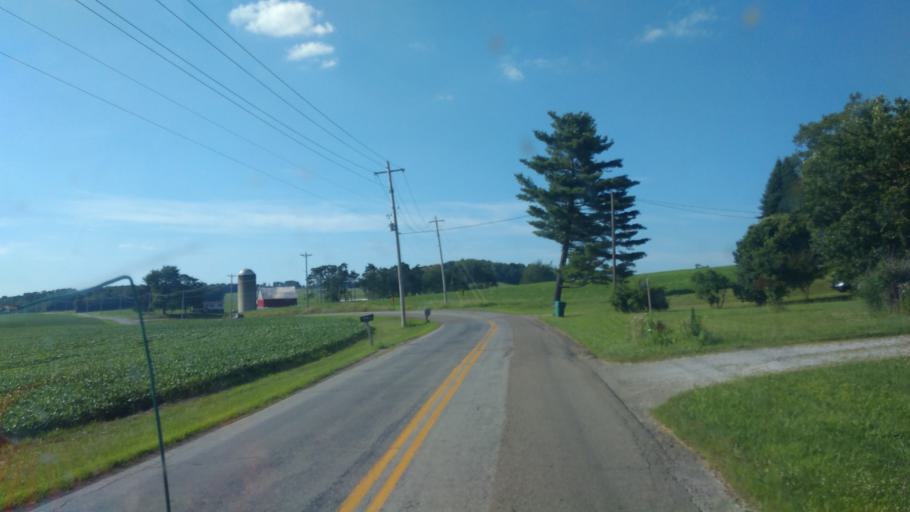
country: US
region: Ohio
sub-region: Wayne County
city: Shreve
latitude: 40.7261
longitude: -82.0532
